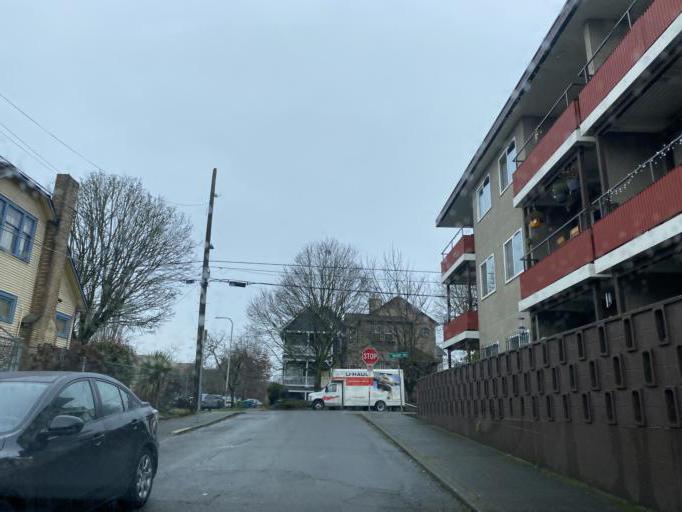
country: US
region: Washington
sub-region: King County
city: Seattle
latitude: 47.6013
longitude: -122.2958
